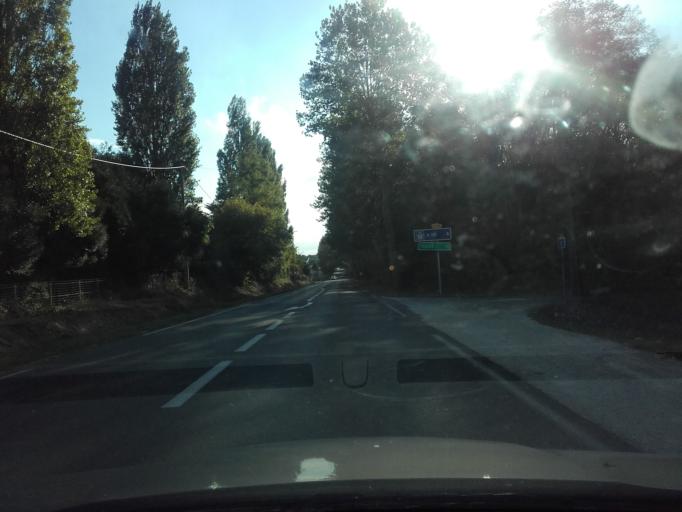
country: FR
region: Centre
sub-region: Departement d'Indre-et-Loire
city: Monnaie
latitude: 47.4966
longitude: 0.7827
